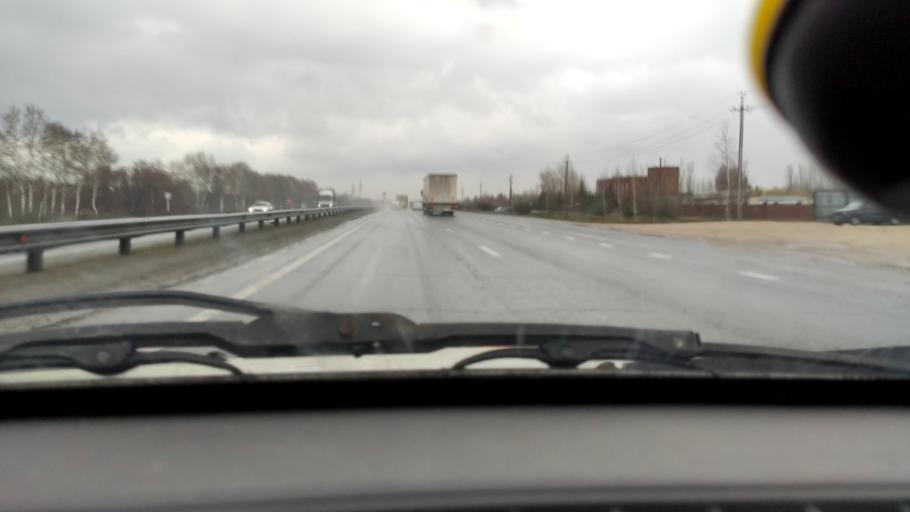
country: RU
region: Samara
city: Tol'yatti
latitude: 53.5780
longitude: 49.4216
